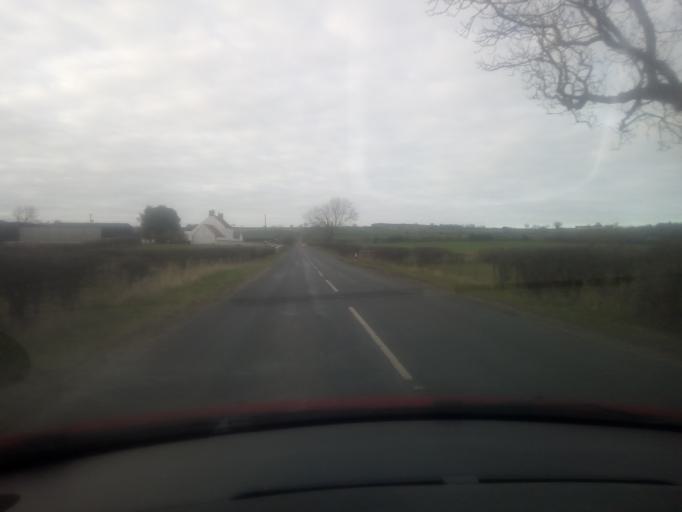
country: GB
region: England
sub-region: Darlington
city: Summerhouse
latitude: 54.5832
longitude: -1.6789
